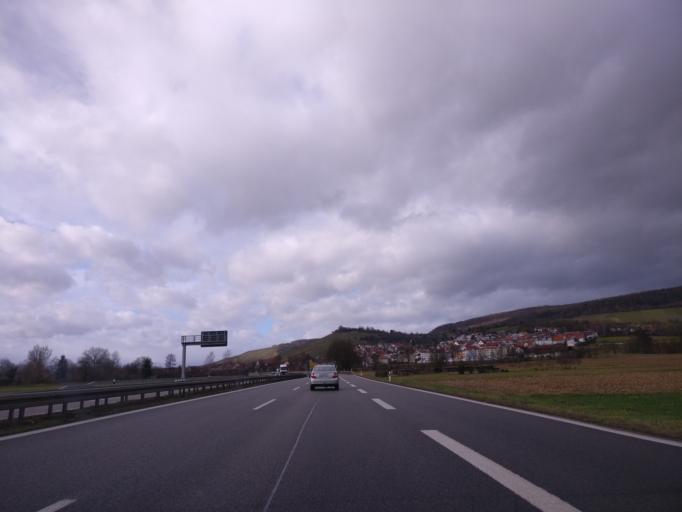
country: DE
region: Baden-Wuerttemberg
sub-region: Regierungsbezirk Stuttgart
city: Winterbach
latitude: 48.8110
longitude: 9.4310
